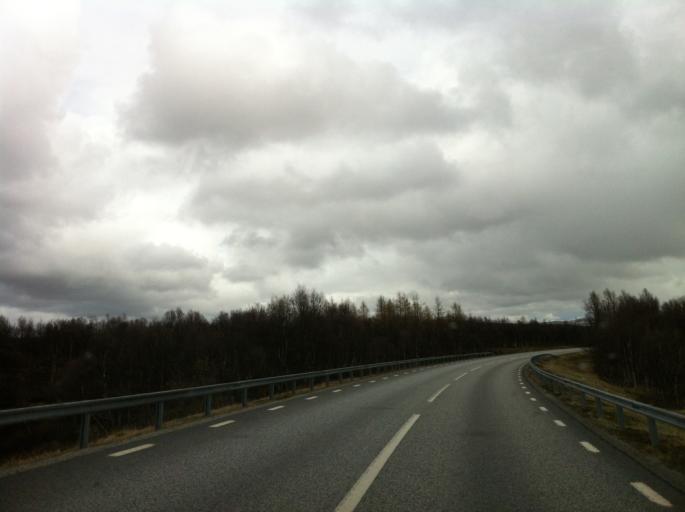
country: NO
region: Sor-Trondelag
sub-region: Tydal
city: Aas
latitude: 62.6402
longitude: 12.0978
